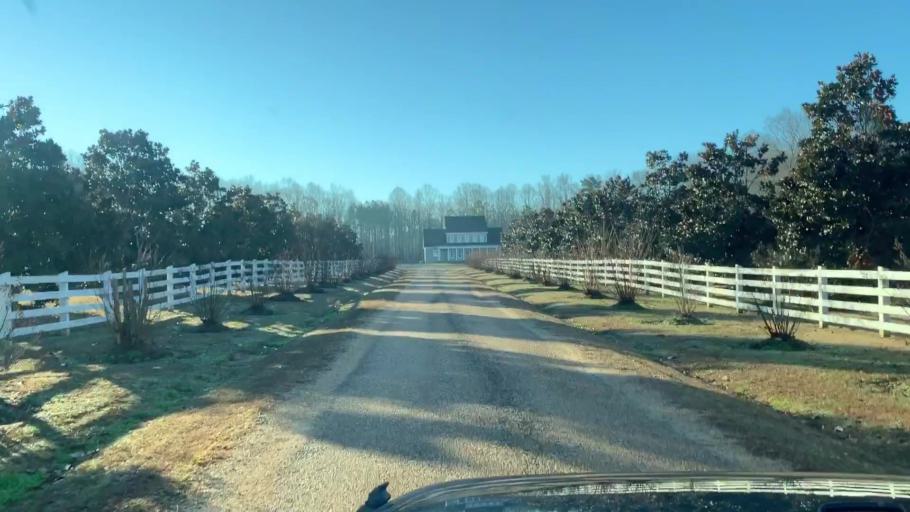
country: US
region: Virginia
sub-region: James City County
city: Williamsburg
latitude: 37.3837
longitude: -76.8206
